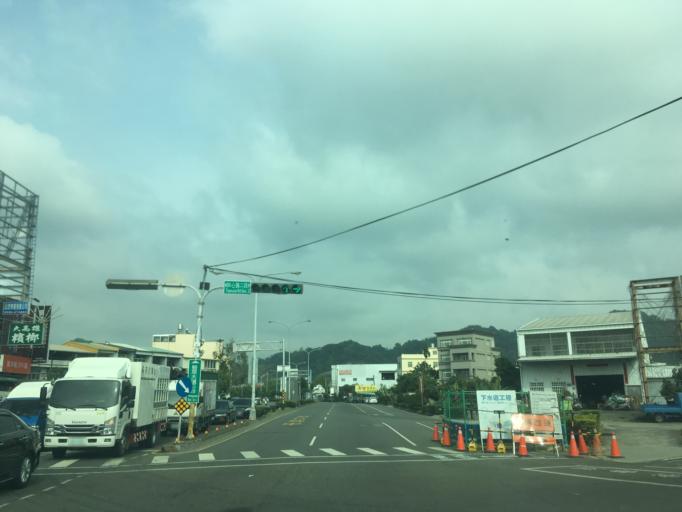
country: TW
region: Taiwan
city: Fengyuan
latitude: 24.2364
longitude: 120.7224
